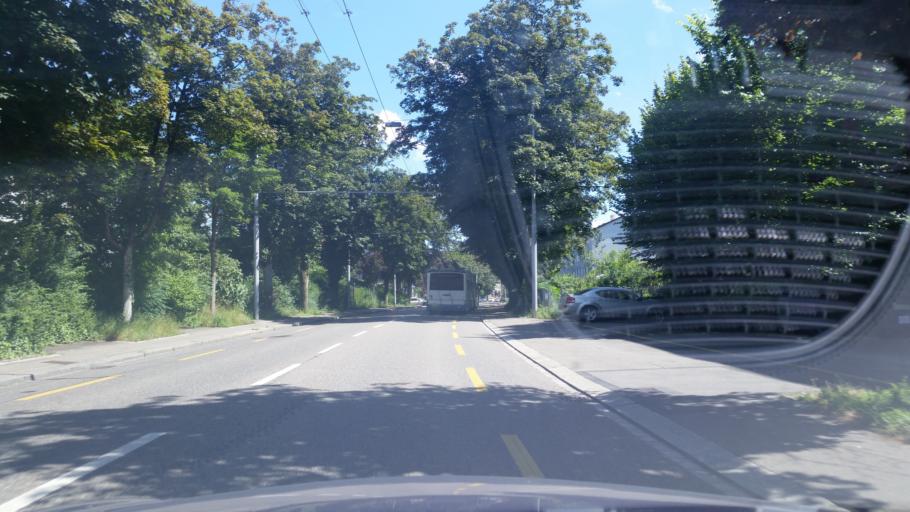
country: CH
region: Zurich
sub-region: Bezirk Zuerich
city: Zuerich (Kreis 11)
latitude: 47.4101
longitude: 8.5277
